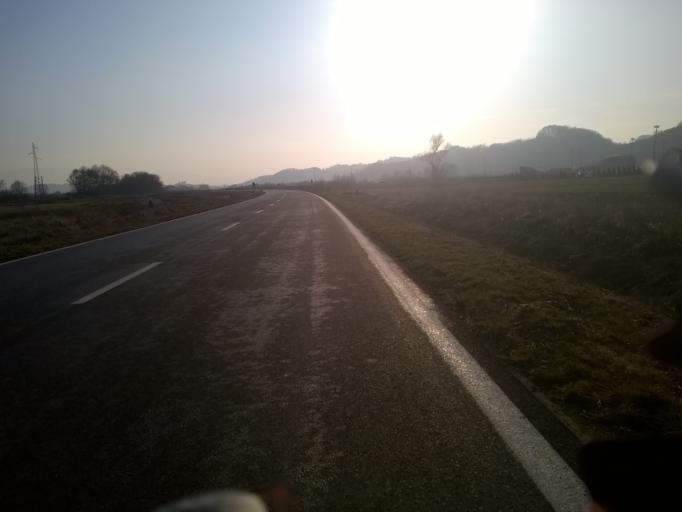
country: HR
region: Krapinsko-Zagorska
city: Zabok
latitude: 46.0693
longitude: 15.9139
